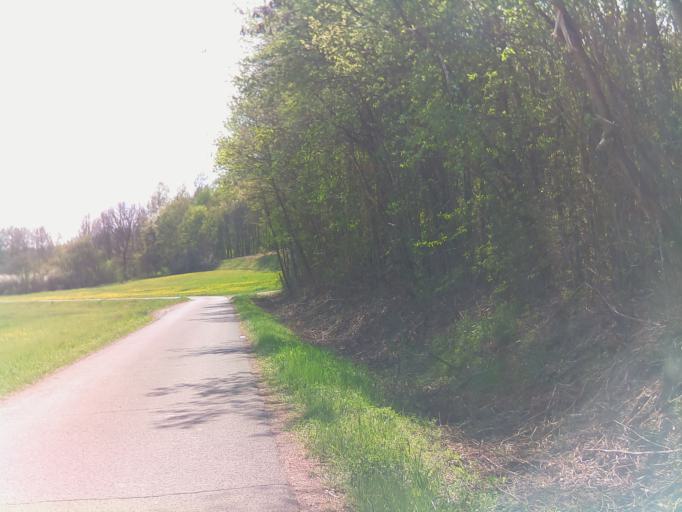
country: DE
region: Bavaria
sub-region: Upper Franconia
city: Weitramsdorf
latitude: 50.2973
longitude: 10.7919
